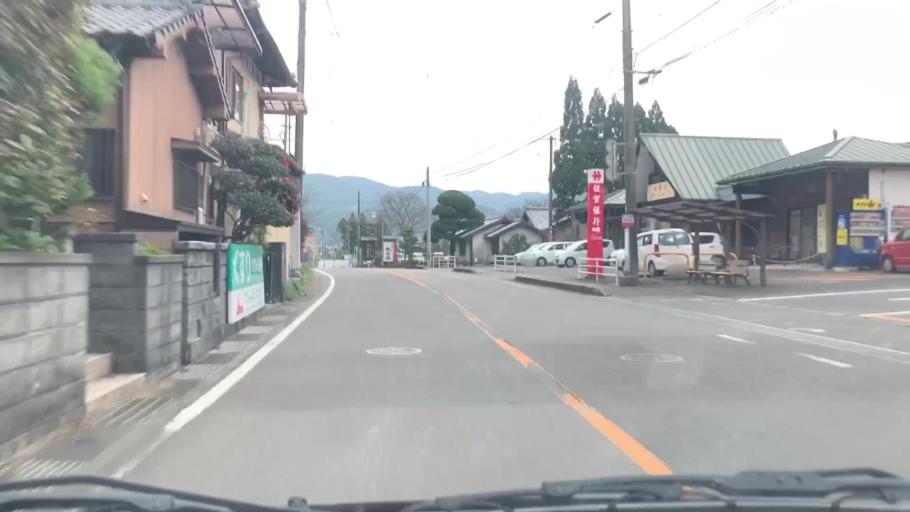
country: JP
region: Saga Prefecture
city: Ureshinomachi-shimojuku
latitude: 33.1019
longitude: 129.9781
